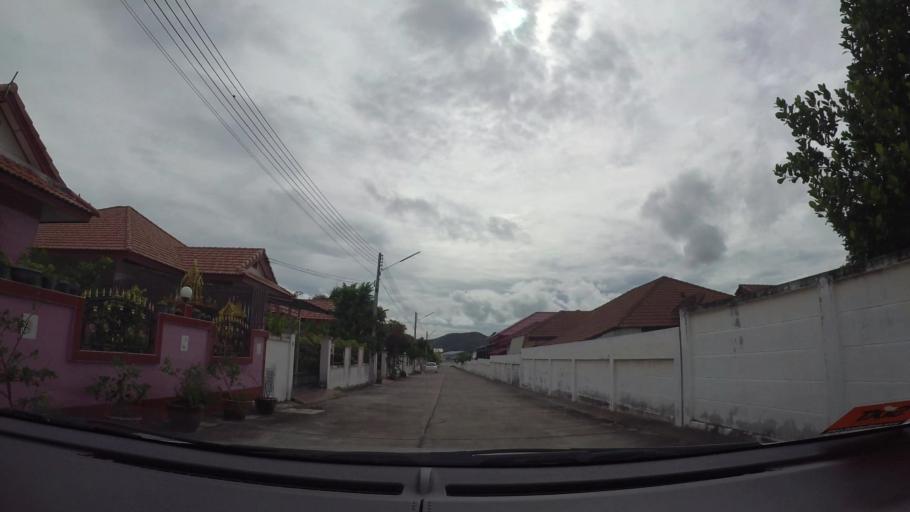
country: TH
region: Chon Buri
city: Sattahip
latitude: 12.7083
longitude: 100.8954
